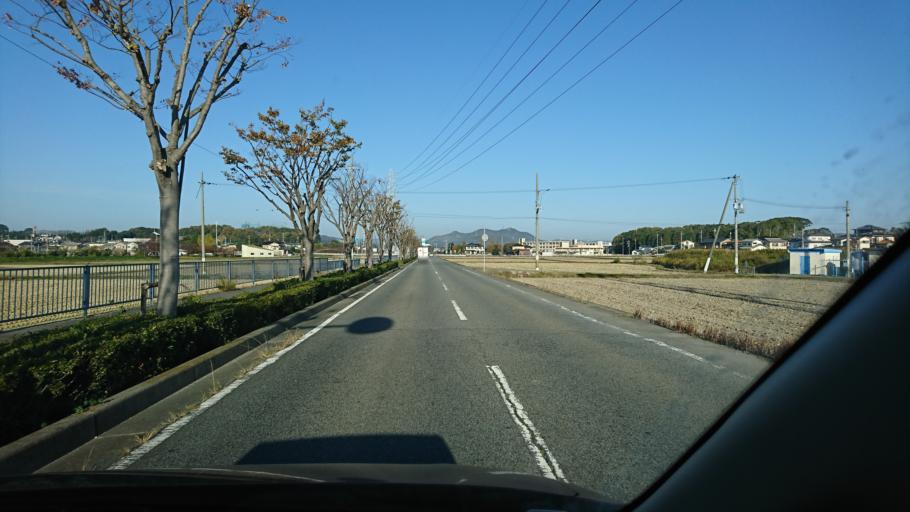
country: JP
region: Hyogo
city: Kakogawacho-honmachi
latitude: 34.7716
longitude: 134.8810
